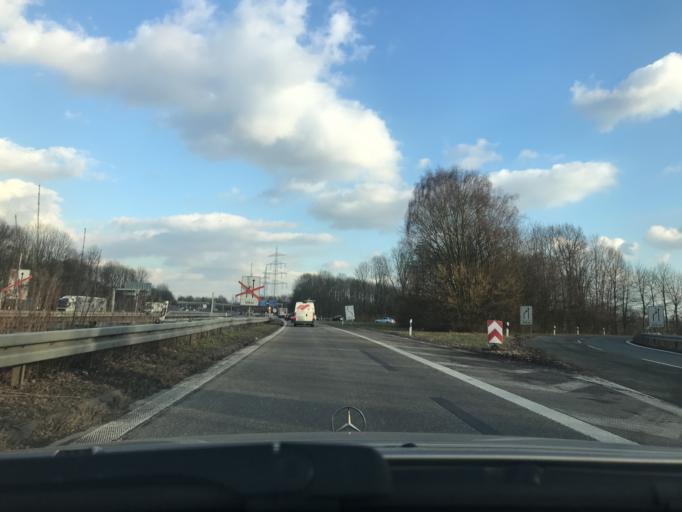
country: DE
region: North Rhine-Westphalia
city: Witten
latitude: 51.4620
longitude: 7.2845
